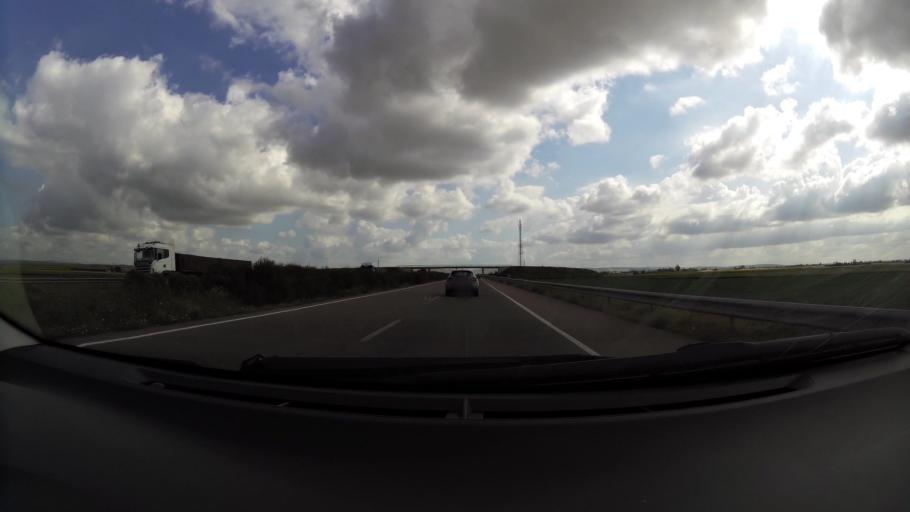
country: MA
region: Chaouia-Ouardigha
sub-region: Settat Province
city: Berrechid
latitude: 33.1380
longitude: -7.5764
